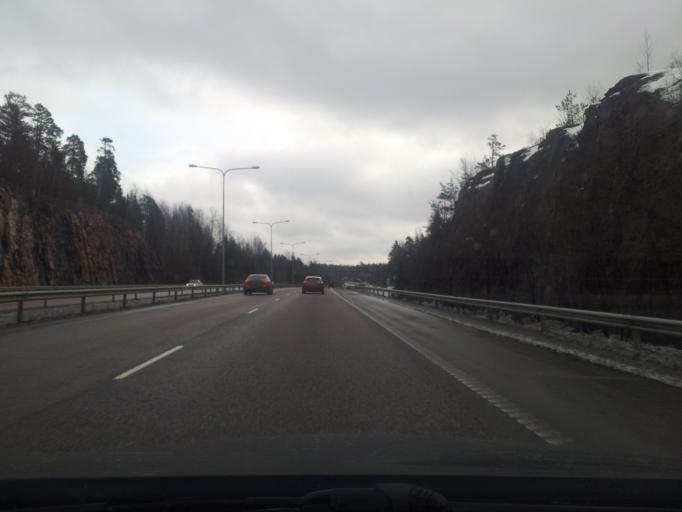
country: FI
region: Uusimaa
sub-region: Helsinki
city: Kauniainen
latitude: 60.2066
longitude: 24.6932
